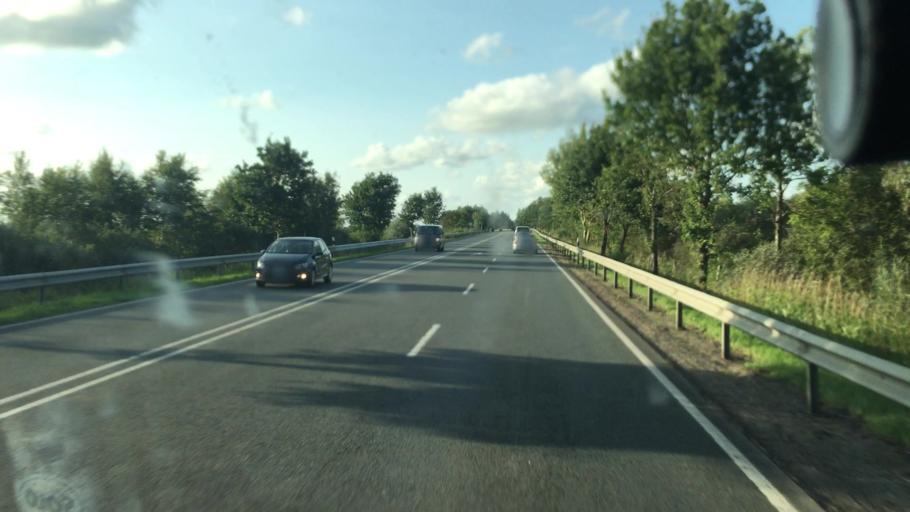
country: DE
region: Lower Saxony
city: Jever
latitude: 53.5752
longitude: 7.9304
